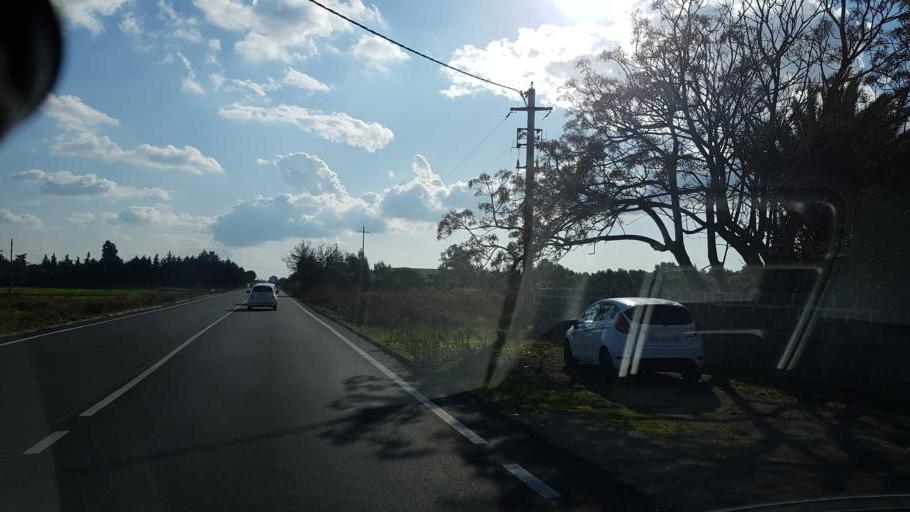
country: IT
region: Apulia
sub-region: Provincia di Lecce
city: Salice Salentino
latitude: 40.3707
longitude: 17.9669
